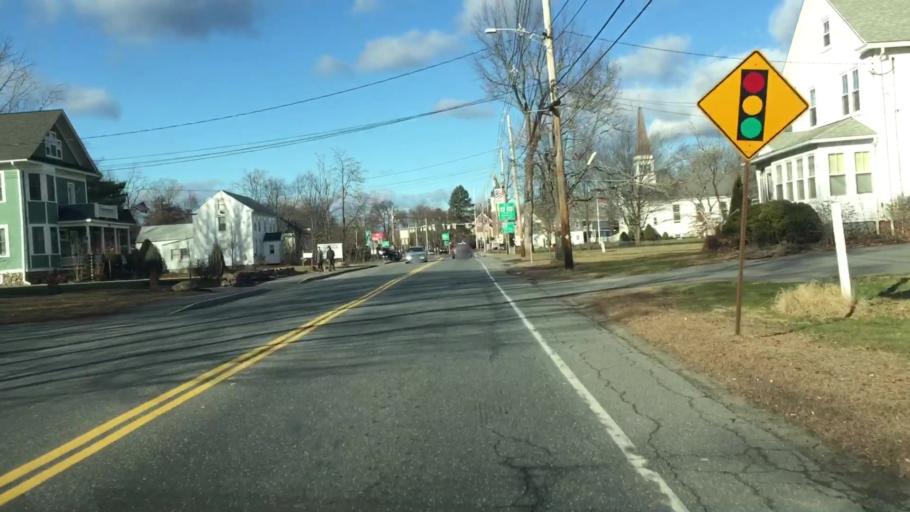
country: US
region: Massachusetts
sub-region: Worcester County
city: West Boylston
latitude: 42.3612
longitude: -71.7808
